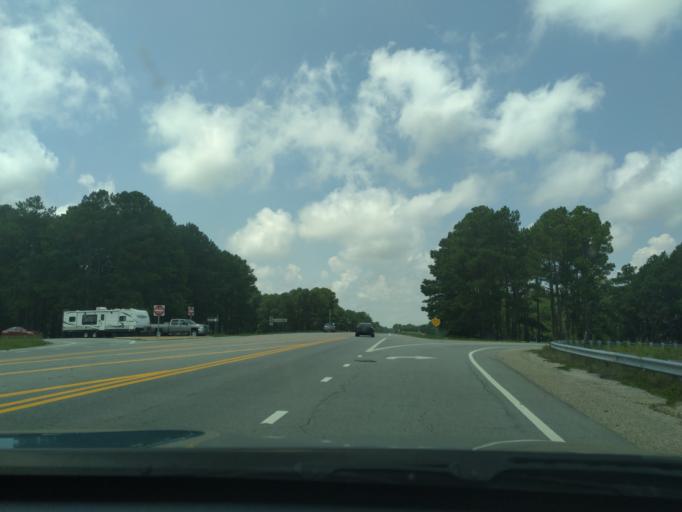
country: US
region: North Carolina
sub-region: Nash County
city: Red Oak
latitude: 36.0131
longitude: -77.8610
